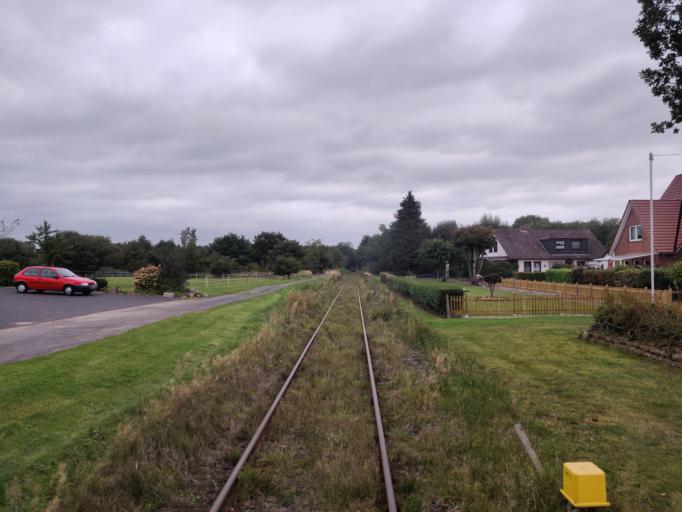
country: DE
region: Lower Saxony
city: Basdahl
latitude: 53.4151
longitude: 9.0140
